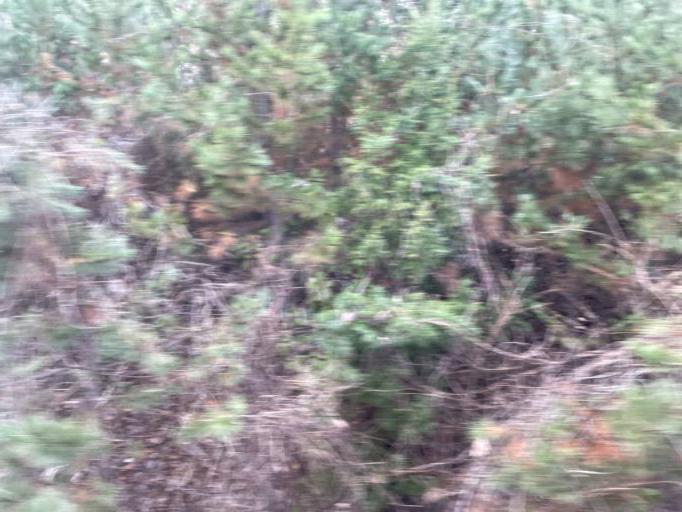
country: JP
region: Aomori
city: Aomori Shi
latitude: 41.0317
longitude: 140.6461
